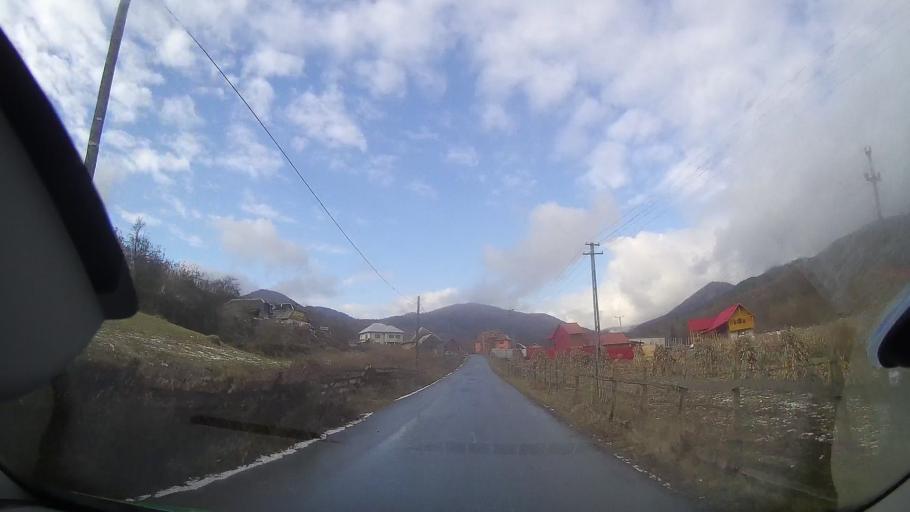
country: RO
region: Alba
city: Salciua de Sus
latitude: 46.4272
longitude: 23.4464
